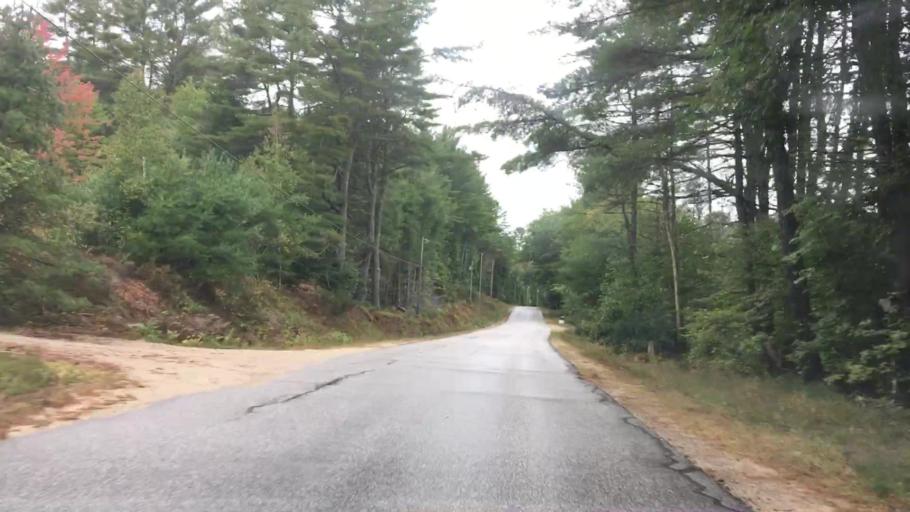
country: US
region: Maine
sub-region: Cumberland County
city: Harrison
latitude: 44.0361
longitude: -70.6034
